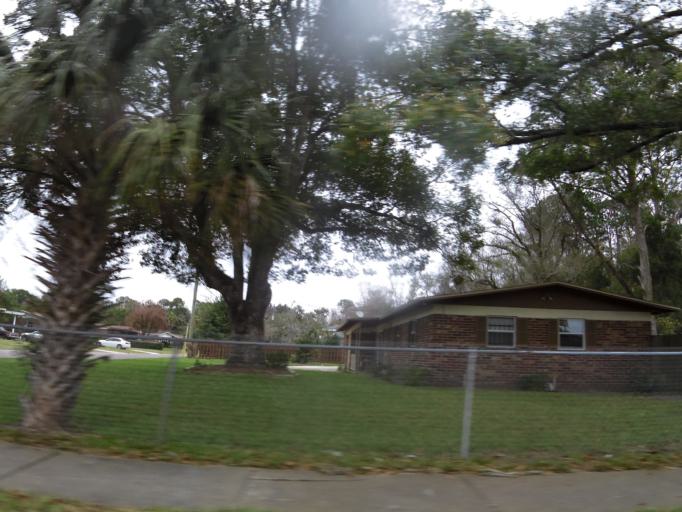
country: US
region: Florida
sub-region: Duval County
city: Jacksonville
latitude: 30.3758
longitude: -81.7147
